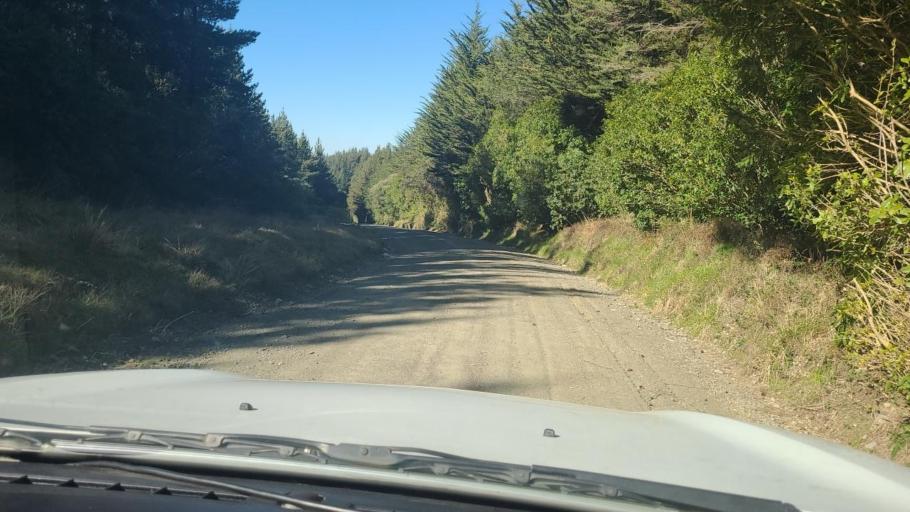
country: NZ
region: Hawke's Bay
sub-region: Napier City
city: Taradale
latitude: -39.4064
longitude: 176.4601
